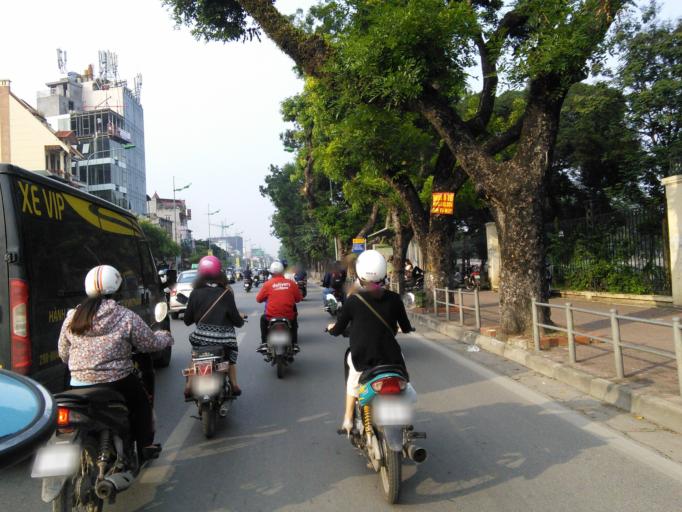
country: VN
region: Ha Noi
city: Hai BaTrung
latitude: 21.0092
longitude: 105.8414
